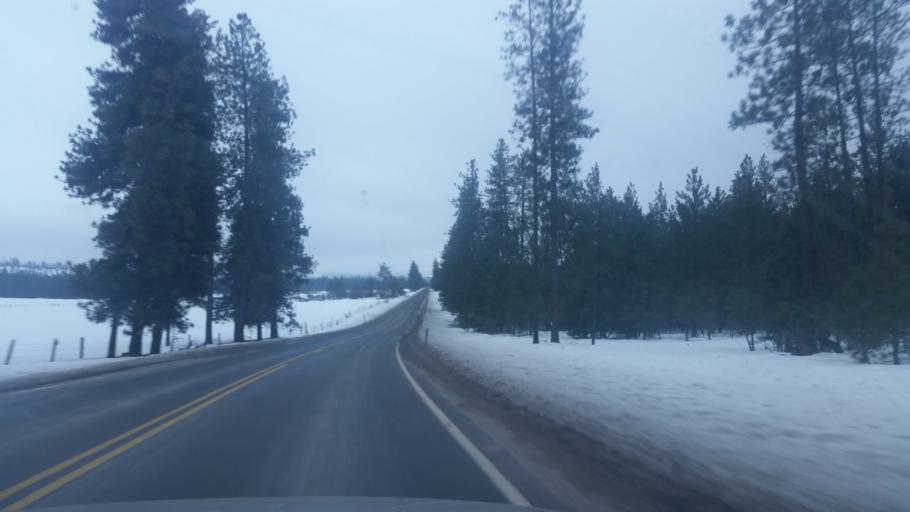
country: US
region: Washington
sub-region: Spokane County
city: Fairchild Air Force Base
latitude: 47.8748
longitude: -117.8379
